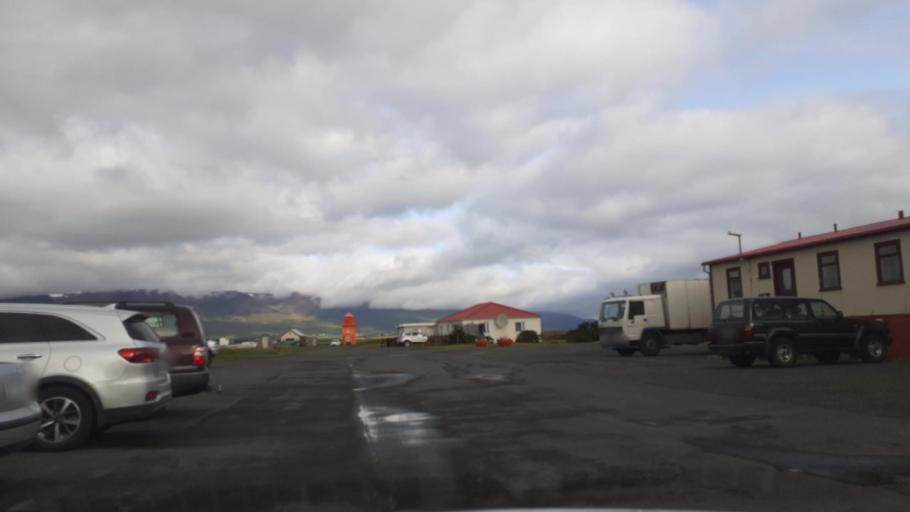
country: IS
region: Northeast
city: Akureyri
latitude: 65.7431
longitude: -18.0882
